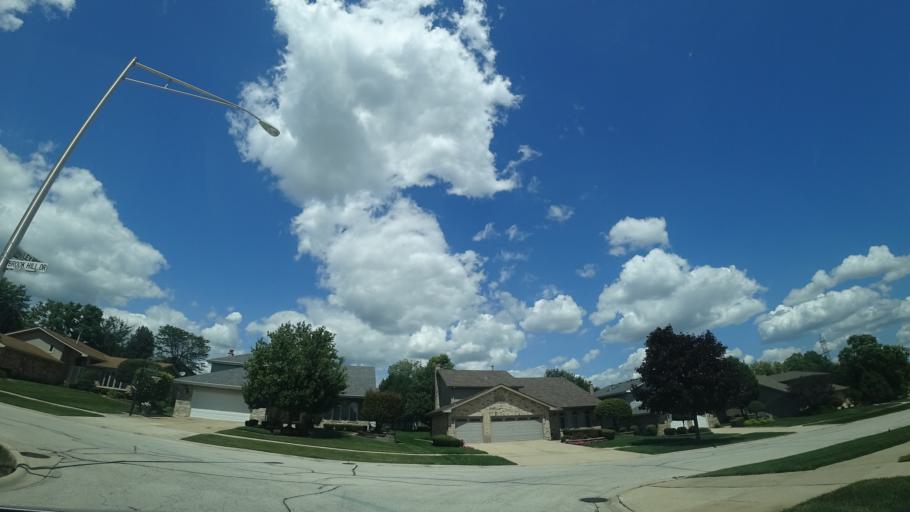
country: US
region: Illinois
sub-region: Will County
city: Homer Glen
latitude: 41.5754
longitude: -87.9025
